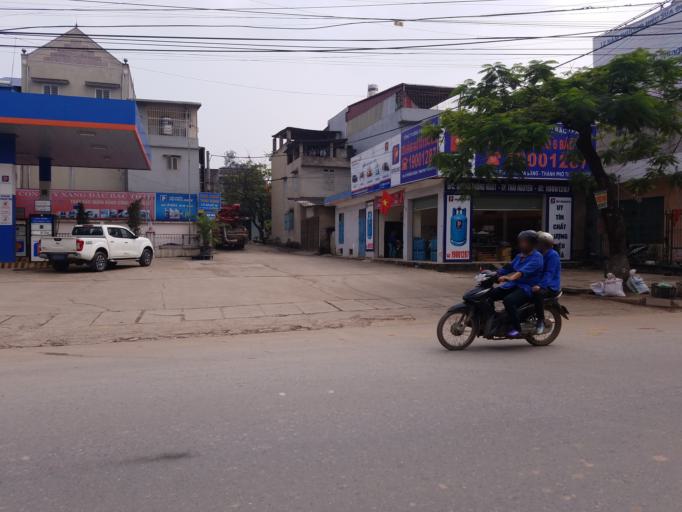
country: VN
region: Thai Nguyen
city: Thanh Pho Thai Nguyen
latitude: 21.5773
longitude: 105.8343
